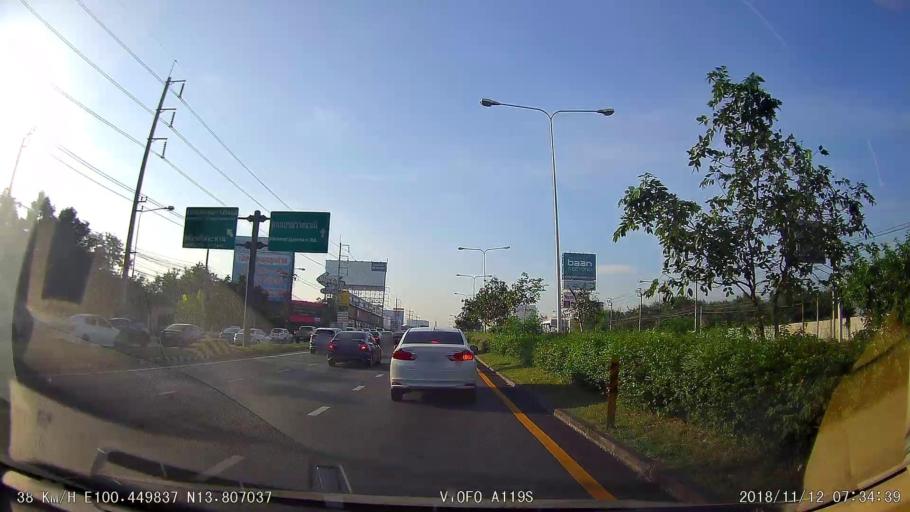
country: TH
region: Nonthaburi
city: Bang Kruai
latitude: 13.8069
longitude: 100.4498
